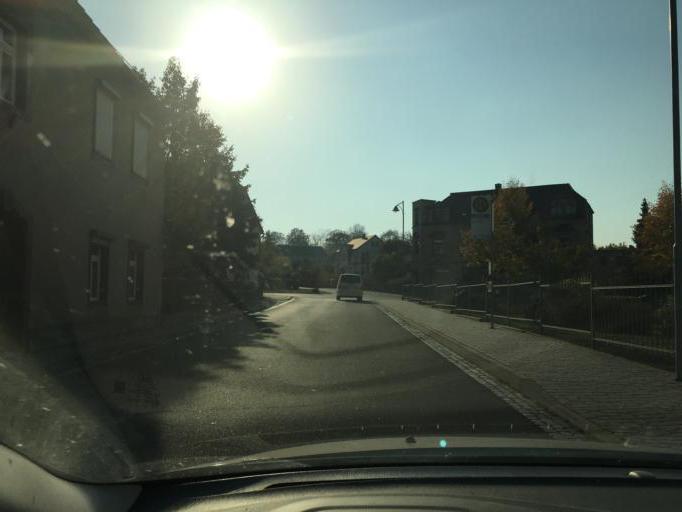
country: DE
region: Saxony
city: Wermsdorf
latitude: 51.2804
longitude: 12.9415
